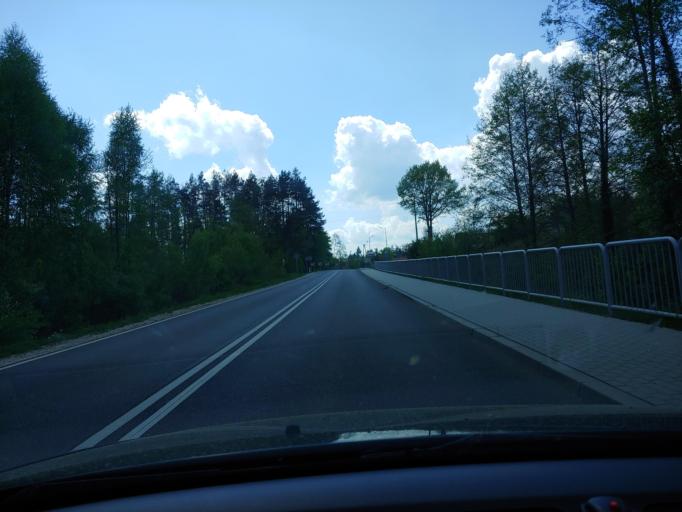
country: PL
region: Lesser Poland Voivodeship
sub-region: Powiat tarnowski
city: Jodlowka-Walki
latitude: 50.1261
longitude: 21.1450
